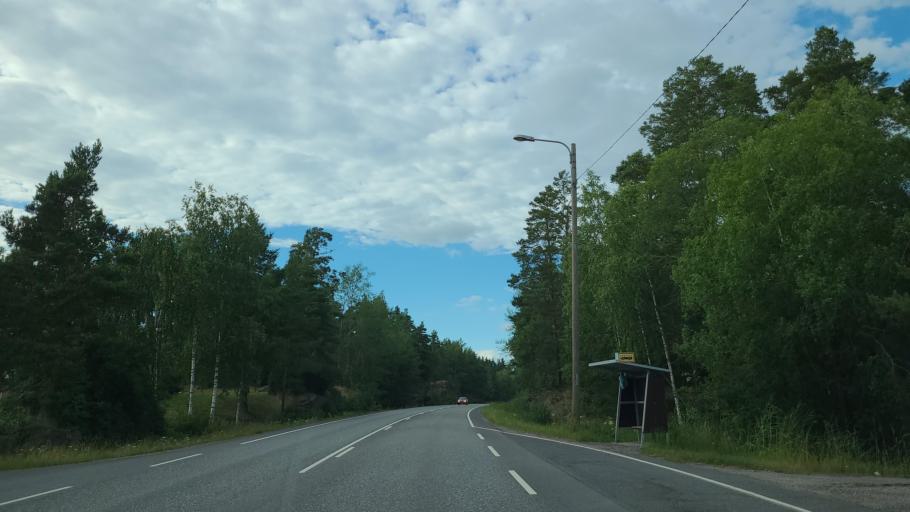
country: FI
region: Varsinais-Suomi
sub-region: Turku
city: Rymaettylae
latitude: 60.4175
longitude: 21.8969
